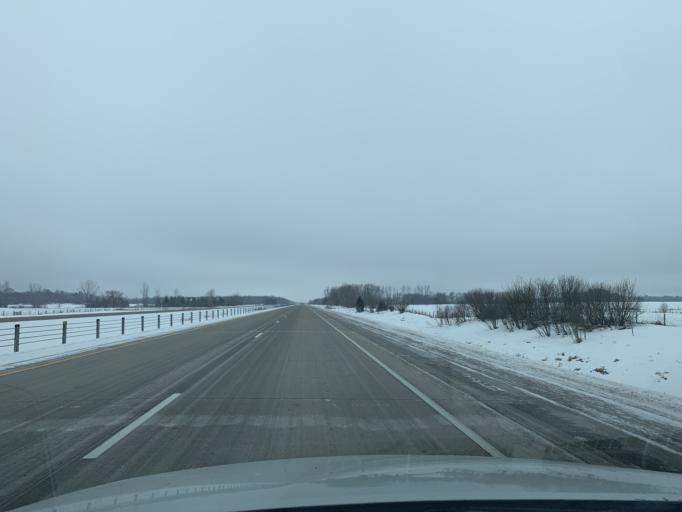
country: US
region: Minnesota
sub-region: Chisago County
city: Rush City
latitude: 45.6514
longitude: -92.9925
